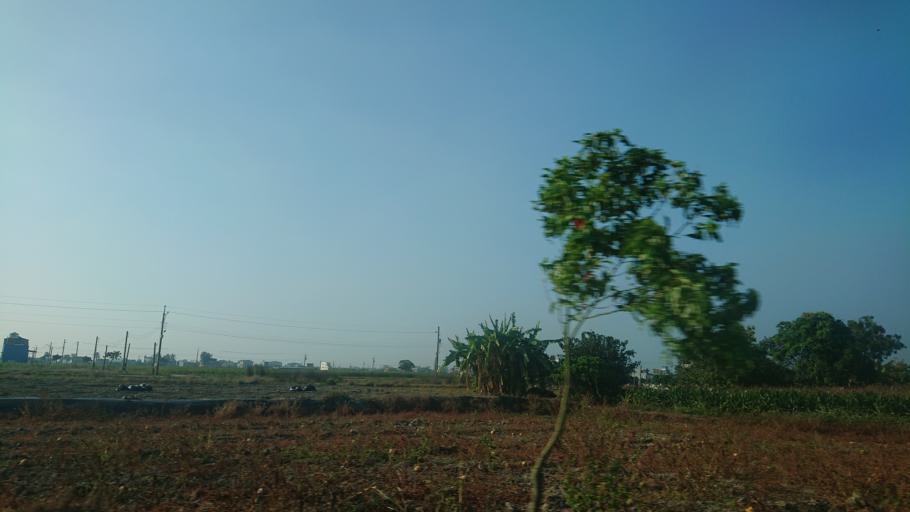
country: TW
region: Taiwan
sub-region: Tainan
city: Tainan
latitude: 23.1302
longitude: 120.2319
